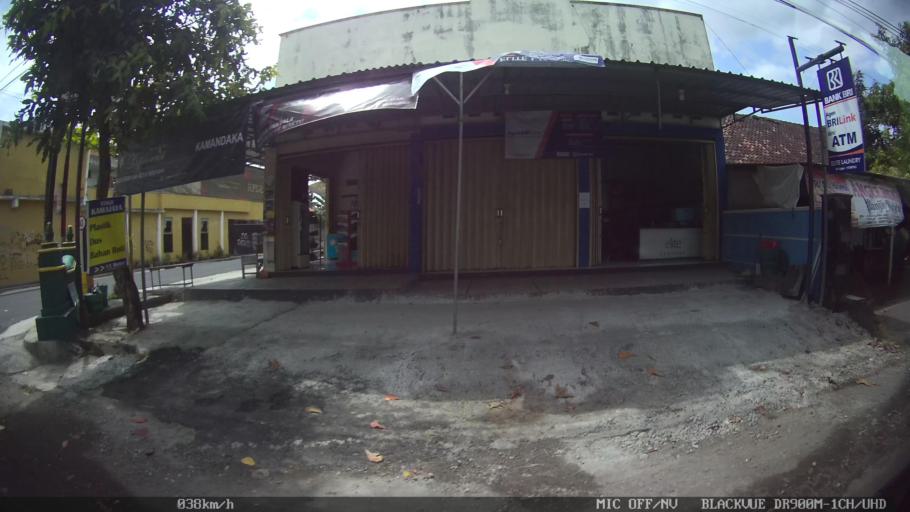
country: ID
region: Daerah Istimewa Yogyakarta
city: Depok
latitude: -7.7886
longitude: 110.4635
